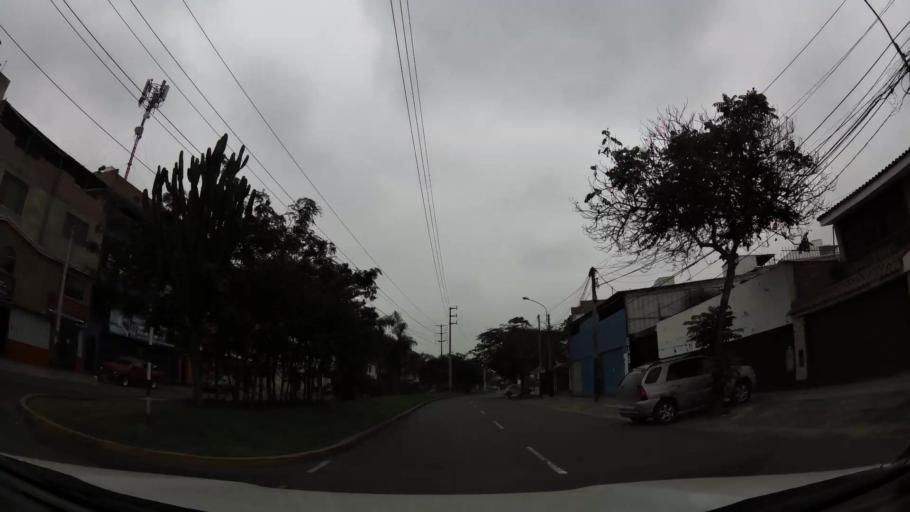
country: PE
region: Lima
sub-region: Lima
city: Surco
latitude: -12.1168
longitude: -76.9963
